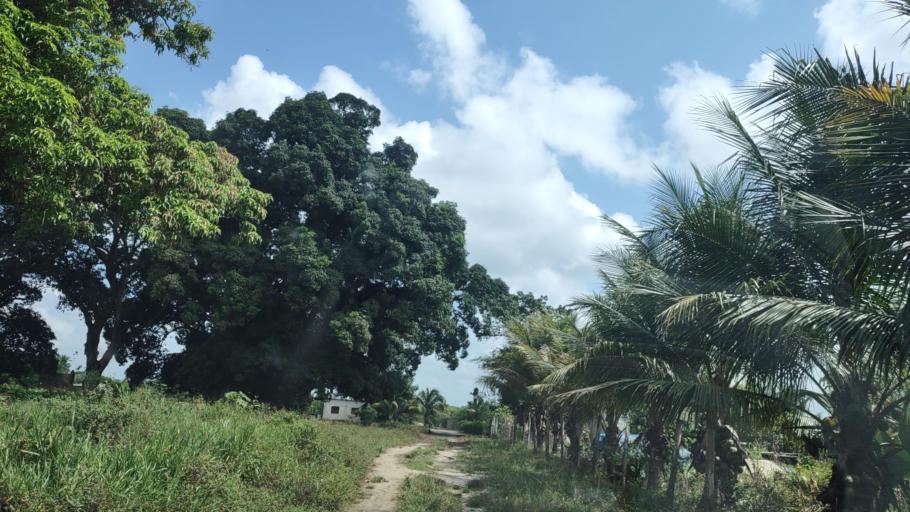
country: MX
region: Veracruz
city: Las Choapas
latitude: 17.9475
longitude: -94.0942
